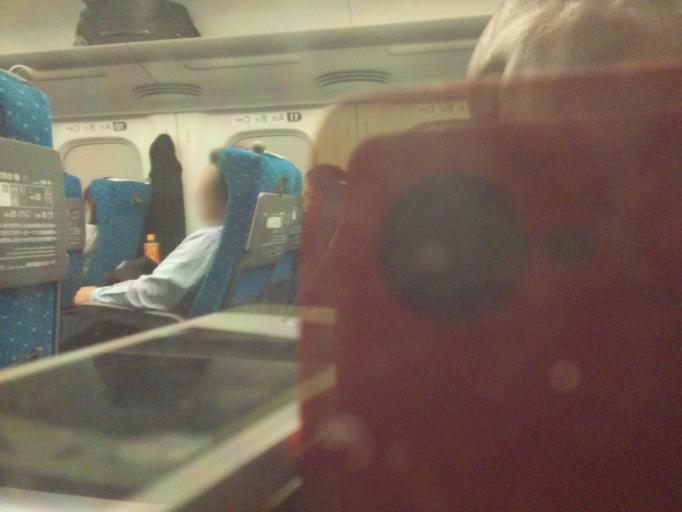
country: JP
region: Shizuoka
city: Yaizu
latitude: 34.9115
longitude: 138.3504
